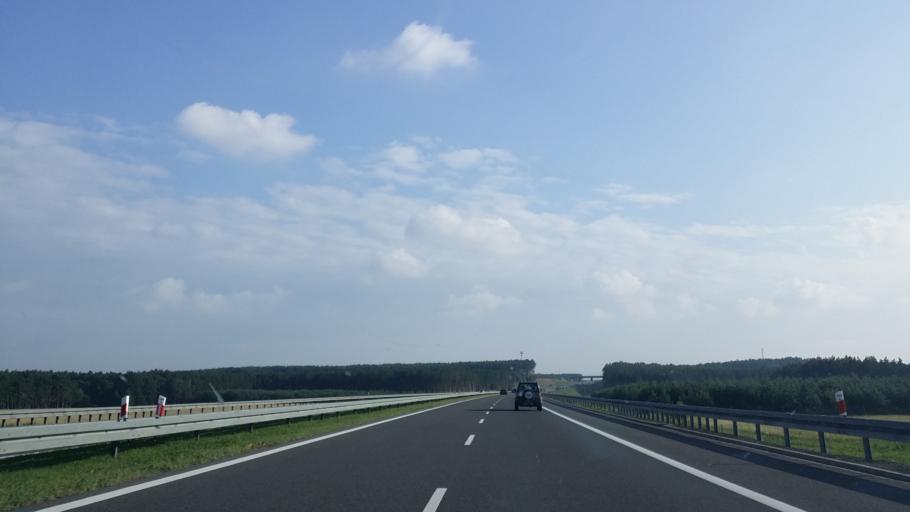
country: PL
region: Lubusz
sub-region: Powiat swiebodzinski
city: Swiebodzin
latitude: 52.3348
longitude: 15.5569
